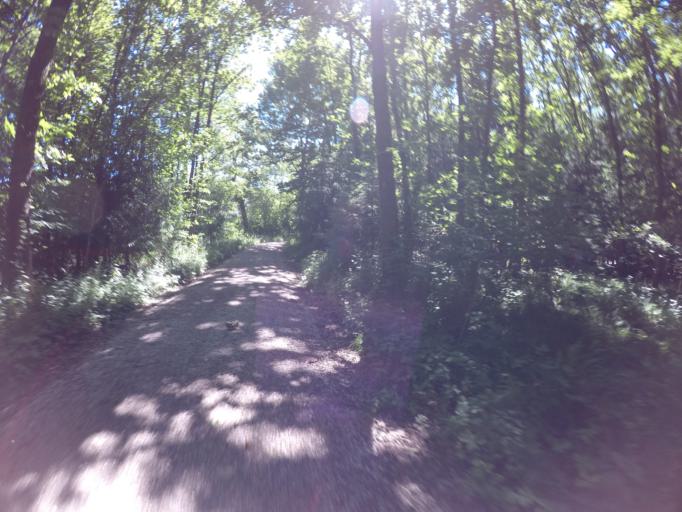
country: DE
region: Bavaria
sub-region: Upper Bavaria
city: Langenbach
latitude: 48.4456
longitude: 11.8396
